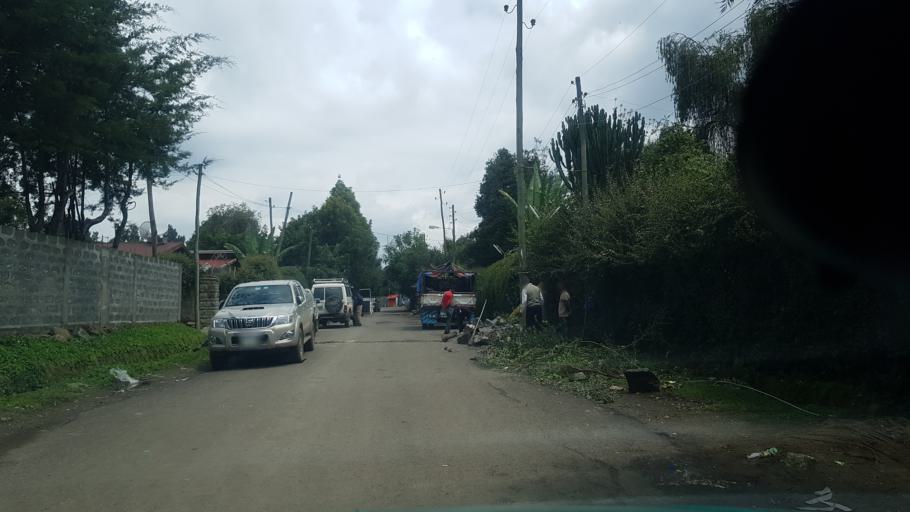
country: ET
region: Adis Abeba
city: Addis Ababa
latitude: 9.0179
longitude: 38.7787
